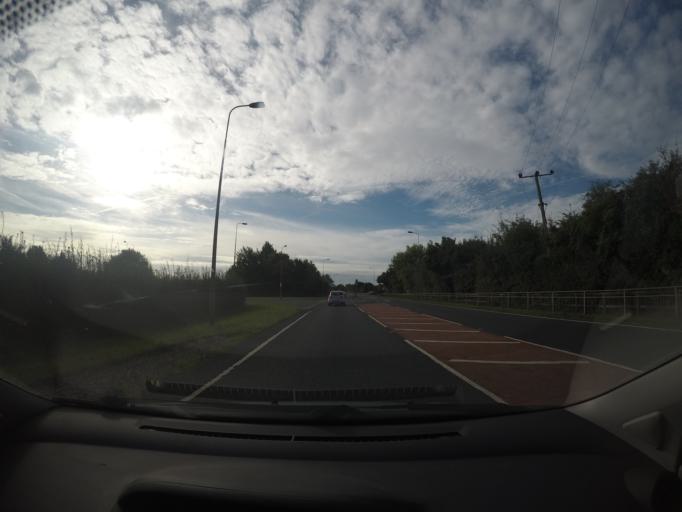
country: GB
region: England
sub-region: North Yorkshire
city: Riccall
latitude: 53.8390
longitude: -1.0556
